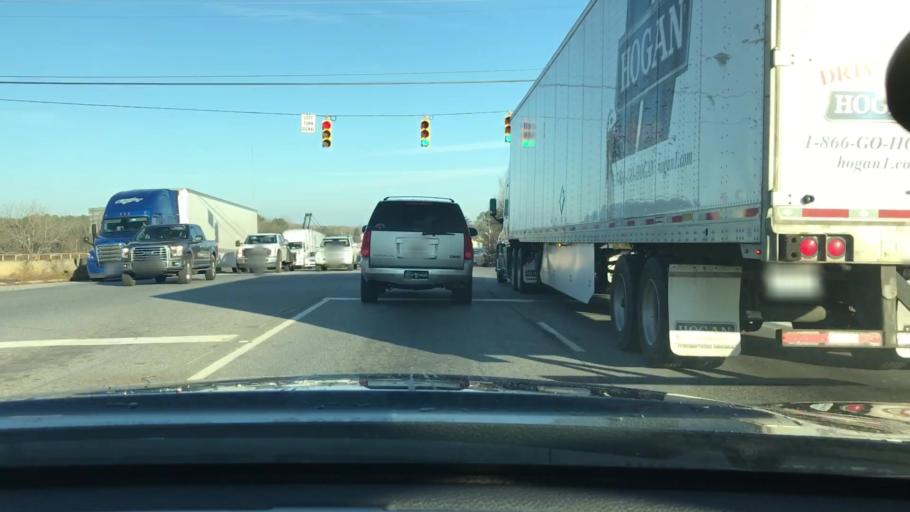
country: US
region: Alabama
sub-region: Talladega County
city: Childersburg
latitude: 33.2771
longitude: -86.3590
